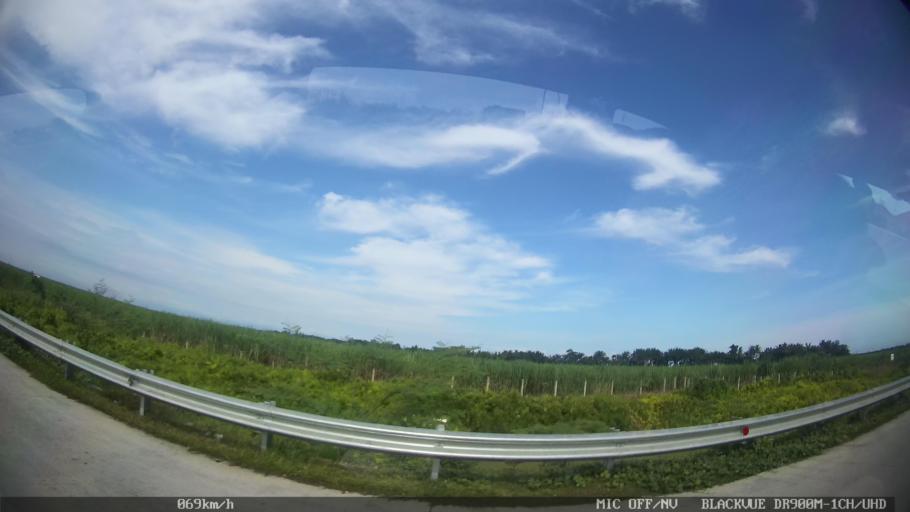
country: ID
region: North Sumatra
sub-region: Kabupaten Langkat
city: Stabat
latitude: 3.7178
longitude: 98.4937
